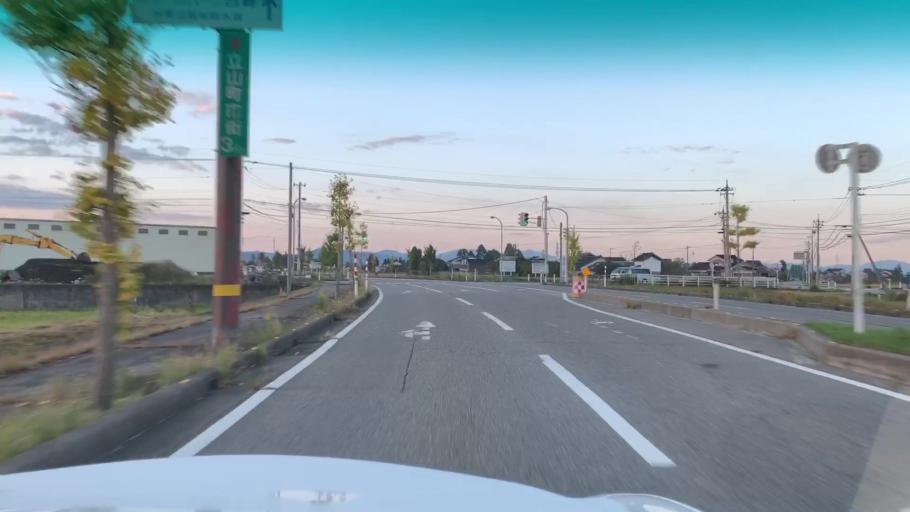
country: JP
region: Toyama
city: Kamiichi
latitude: 36.6797
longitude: 137.3281
